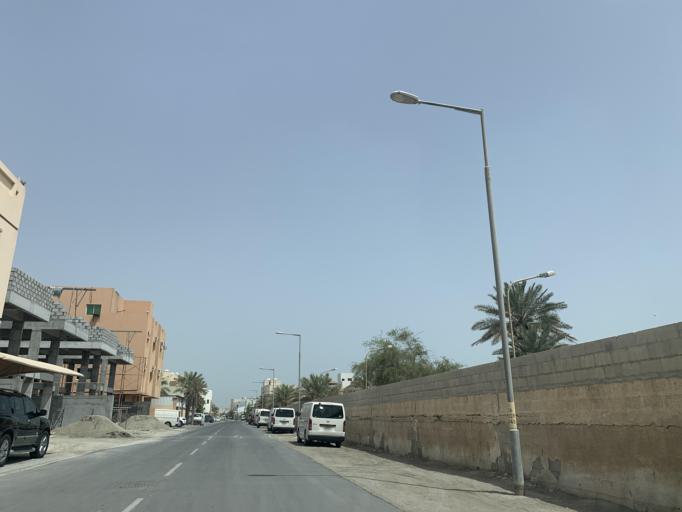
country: BH
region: Northern
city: Sitrah
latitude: 26.1361
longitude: 50.6042
